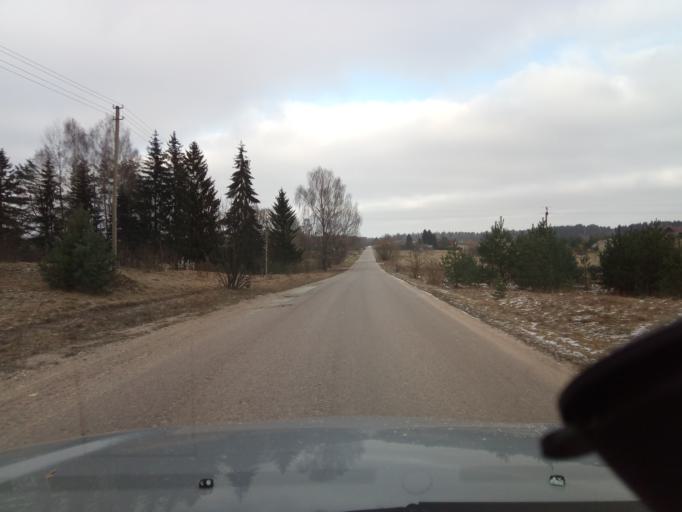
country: LT
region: Alytaus apskritis
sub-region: Alytaus rajonas
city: Daugai
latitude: 54.3479
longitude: 24.2567
